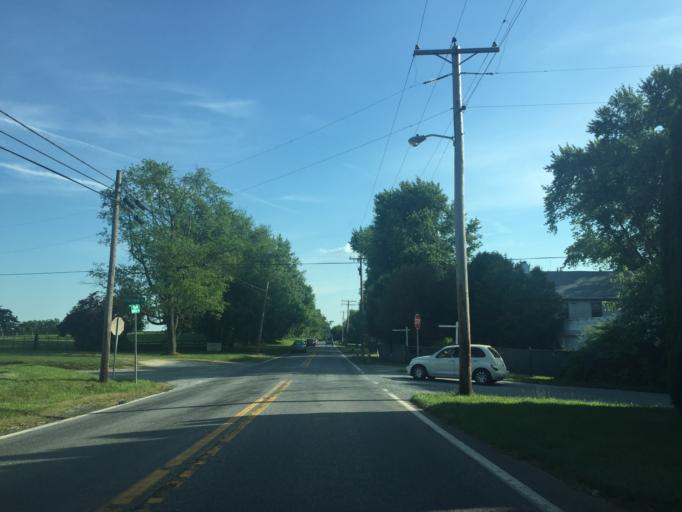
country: US
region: Maryland
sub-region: Harford County
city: Jarrettsville
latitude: 39.5767
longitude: -76.5169
